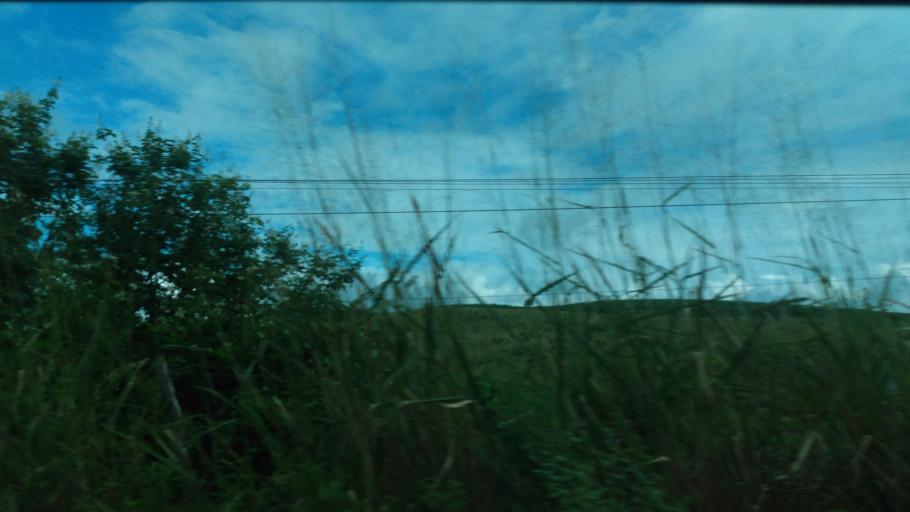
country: BR
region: Pernambuco
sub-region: Catende
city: Catende
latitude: -8.6998
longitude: -35.7410
